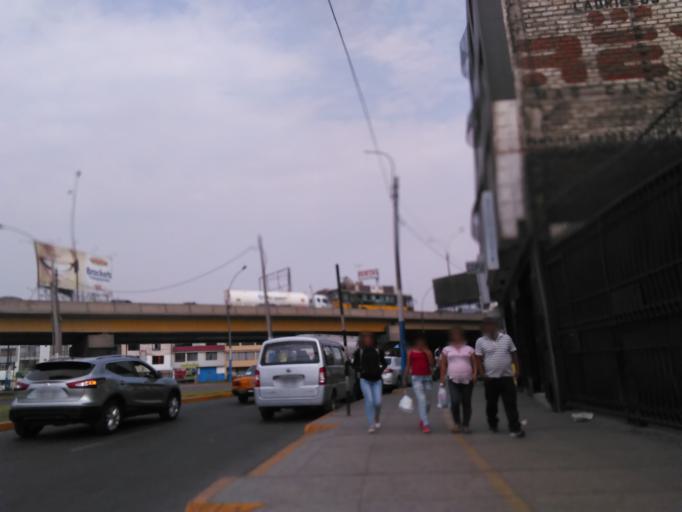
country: PE
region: Lima
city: Lima
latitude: -12.0293
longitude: -77.0583
